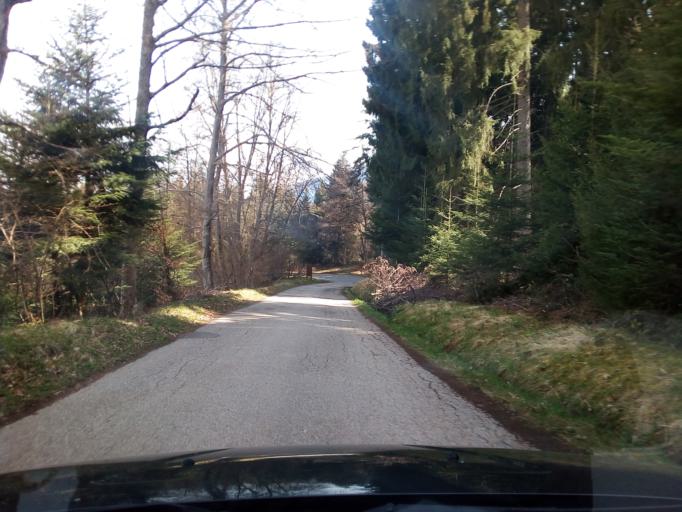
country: FR
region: Rhone-Alpes
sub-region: Departement de l'Isere
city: Revel
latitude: 45.1648
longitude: 5.8651
